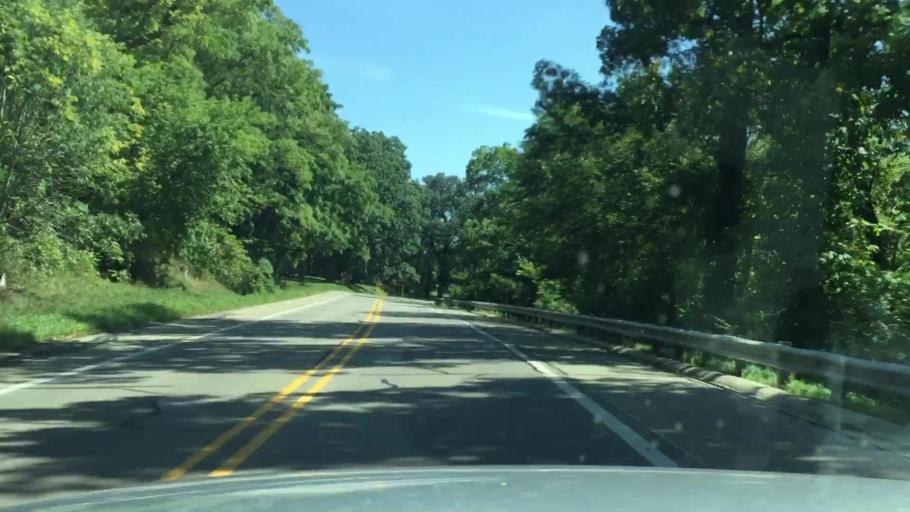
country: US
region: Michigan
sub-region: Jackson County
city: Brooklyn
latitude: 42.0615
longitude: -84.1869
